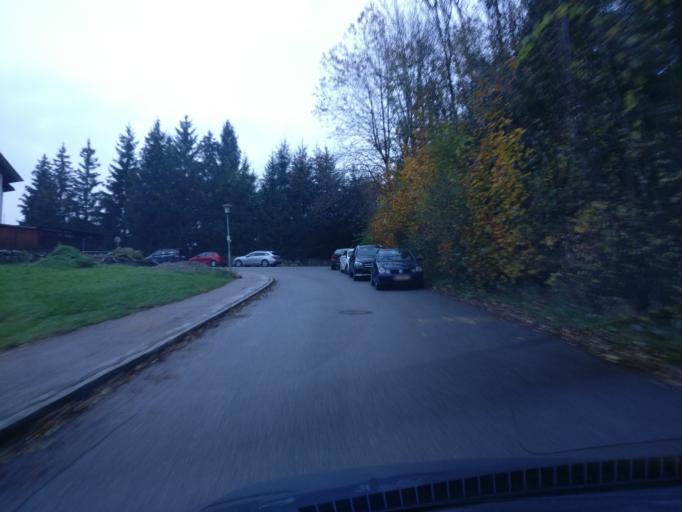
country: AT
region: Salzburg
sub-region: Politischer Bezirk Salzburg-Umgebung
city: Elixhausen
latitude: 47.8627
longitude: 13.0663
